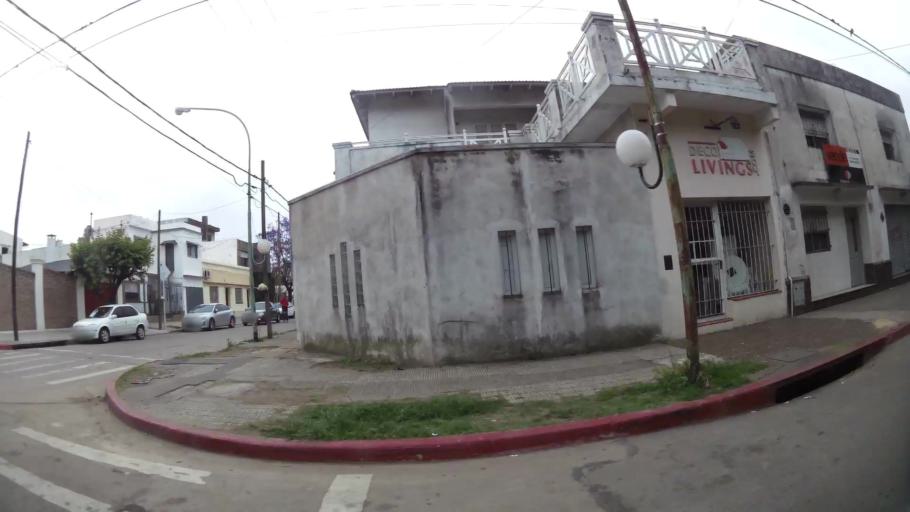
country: AR
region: Buenos Aires
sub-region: Partido de Zarate
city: Zarate
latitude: -34.0928
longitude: -59.0258
